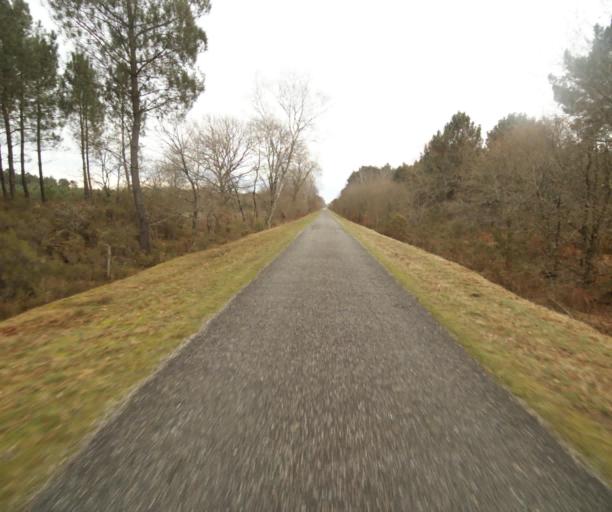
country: FR
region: Aquitaine
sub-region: Departement des Landes
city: Gabarret
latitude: 44.0229
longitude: -0.0481
